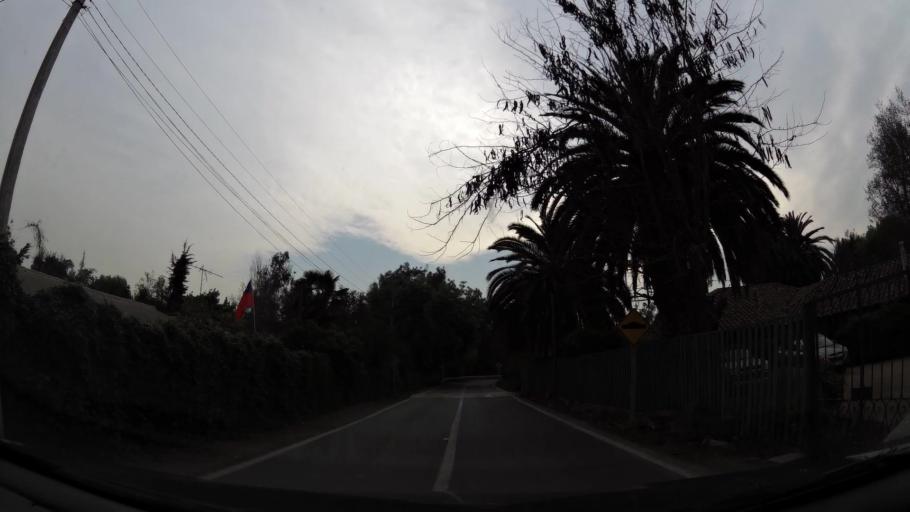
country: CL
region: Santiago Metropolitan
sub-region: Provincia de Chacabuco
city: Chicureo Abajo
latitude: -33.2739
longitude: -70.7020
